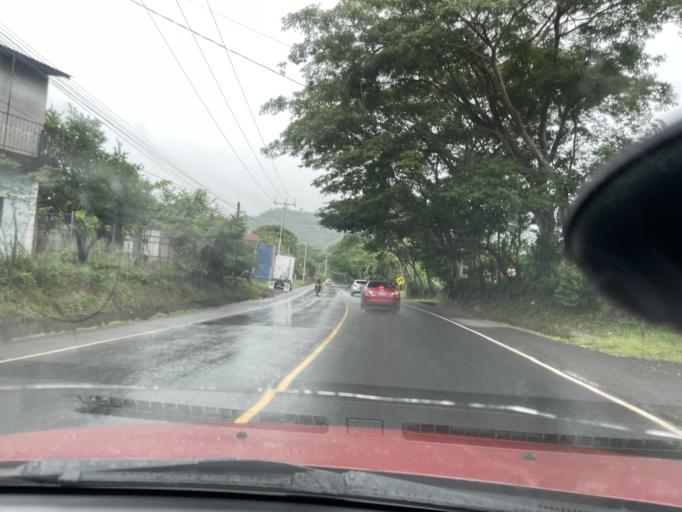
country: SV
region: San Miguel
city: San Miguel
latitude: 13.5483
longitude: -88.1174
